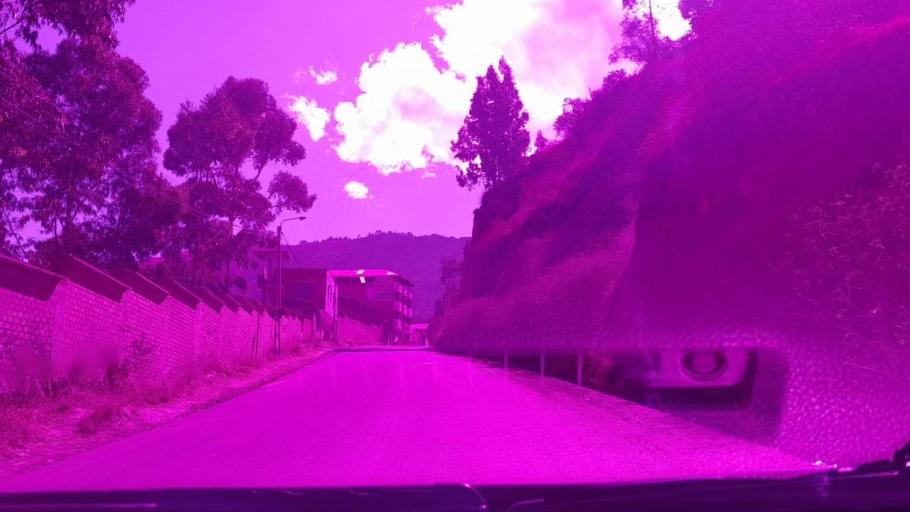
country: PE
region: Cusco
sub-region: Provincia de Cusco
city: Cusco
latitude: -13.5274
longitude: -71.9097
